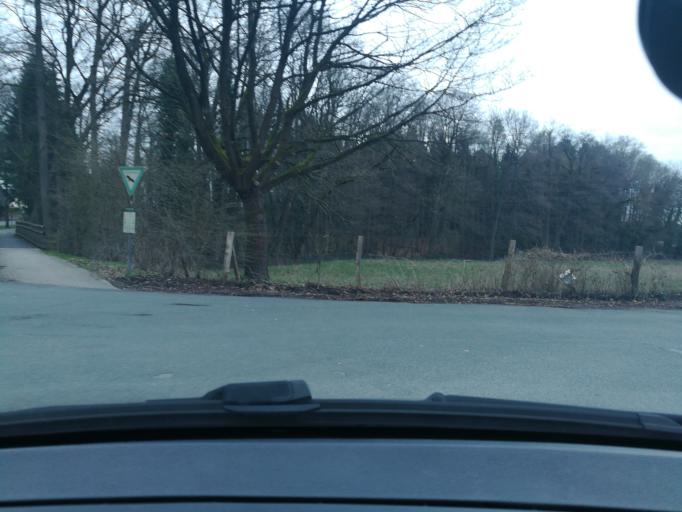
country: DE
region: North Rhine-Westphalia
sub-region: Regierungsbezirk Detmold
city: Oerlinghausen
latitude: 51.9485
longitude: 8.6332
